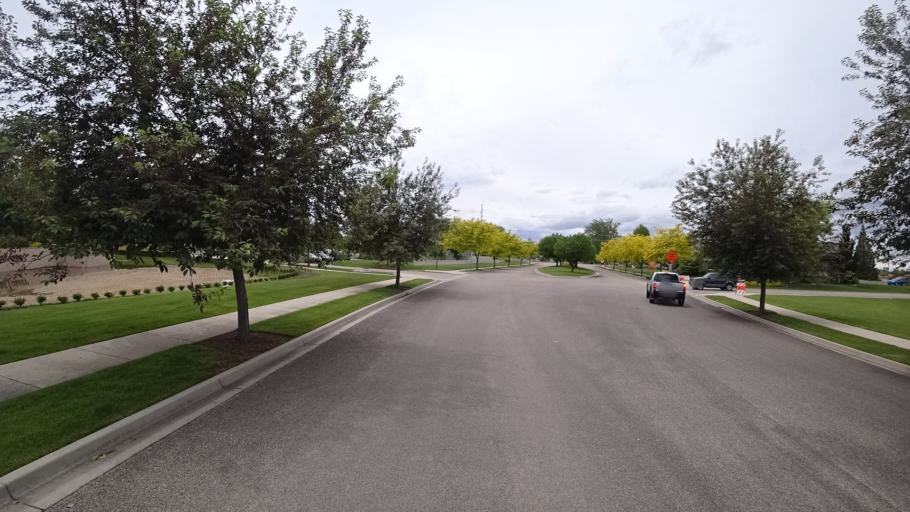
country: US
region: Idaho
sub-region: Ada County
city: Meridian
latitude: 43.6436
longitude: -116.4317
